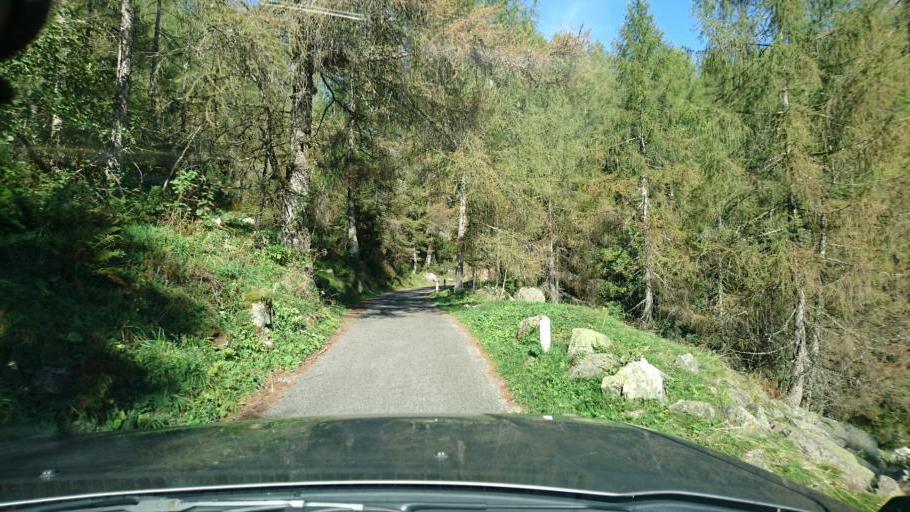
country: IT
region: Lombardy
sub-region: Provincia di Brescia
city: Lozio
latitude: 46.0474
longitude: 10.2232
